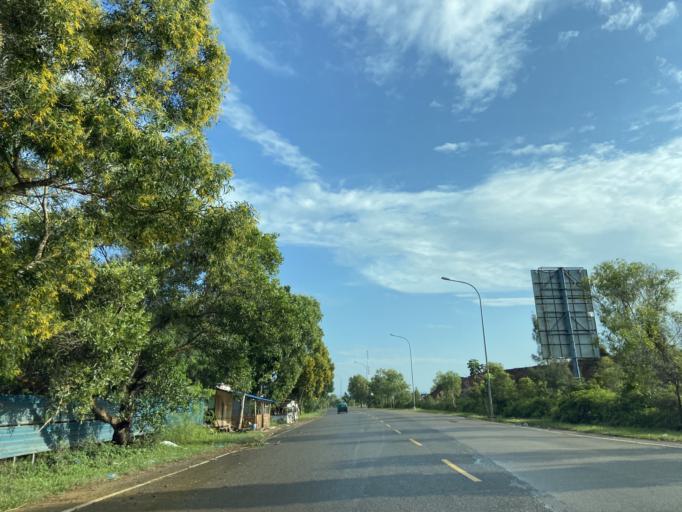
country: SG
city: Singapore
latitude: 0.9694
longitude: 104.0547
